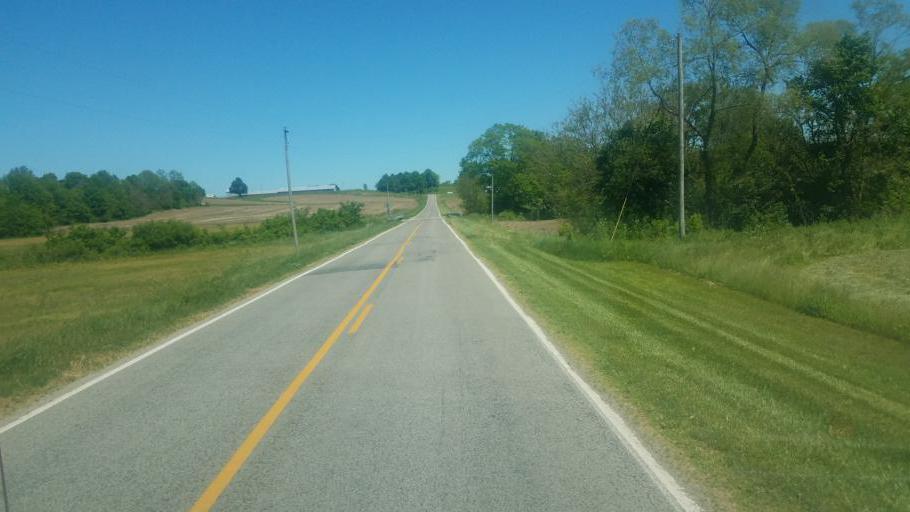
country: US
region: Ohio
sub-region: Champaign County
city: Saint Paris
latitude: 40.2023
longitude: -83.9885
